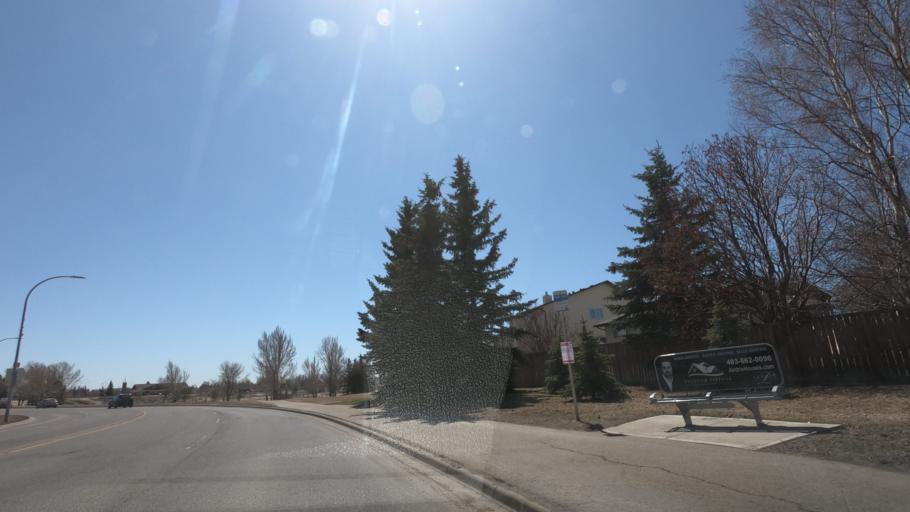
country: CA
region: Alberta
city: Airdrie
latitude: 51.2847
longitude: -114.0135
